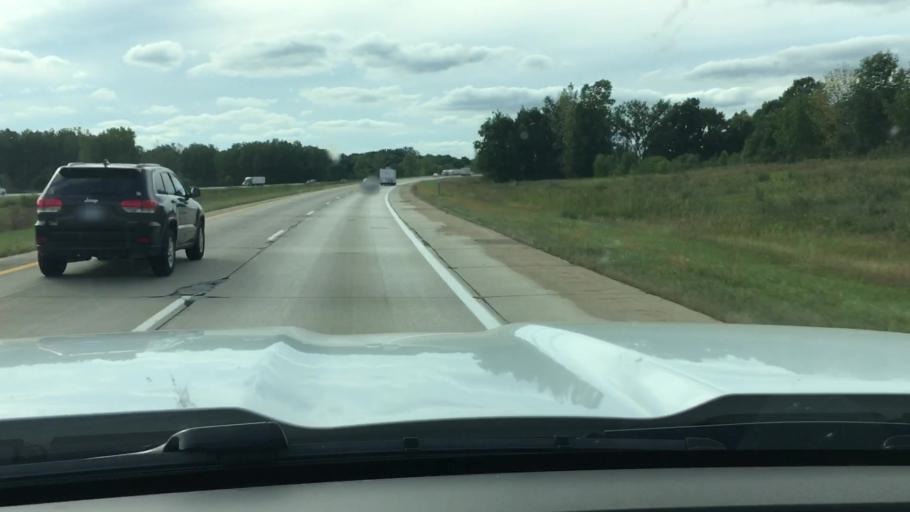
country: US
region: Michigan
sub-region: Lapeer County
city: Imlay City
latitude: 42.9970
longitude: -83.1363
